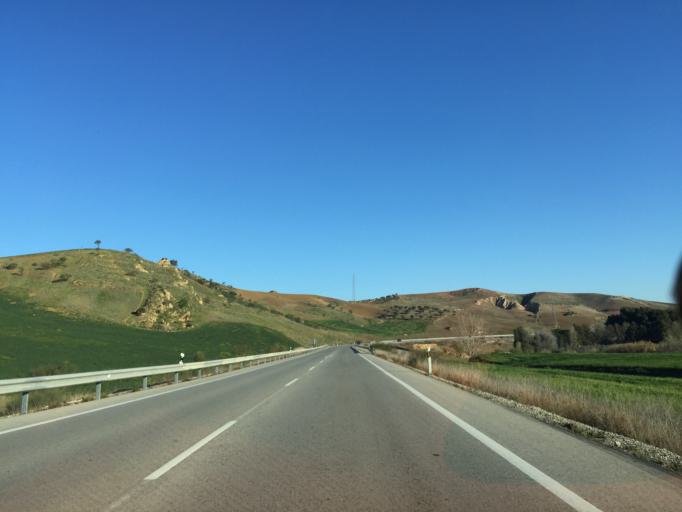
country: ES
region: Andalusia
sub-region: Provincia de Malaga
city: Ardales
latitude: 36.8914
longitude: -4.8481
